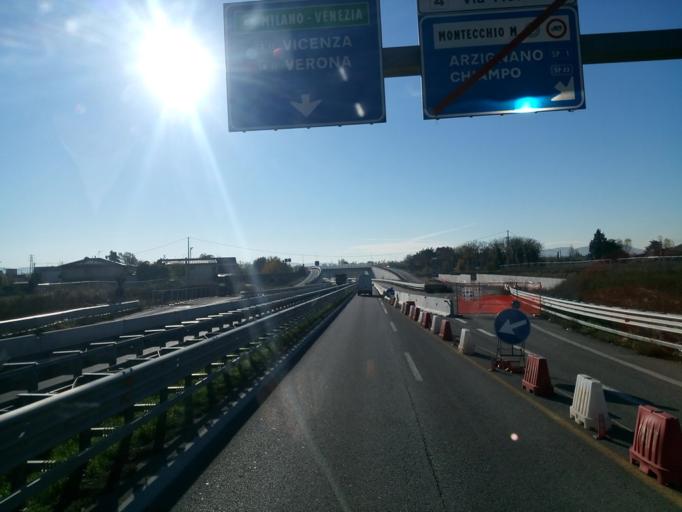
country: IT
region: Veneto
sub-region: Provincia di Vicenza
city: Montecchio Maggiore-Alte Ceccato
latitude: 45.5137
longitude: 11.3876
